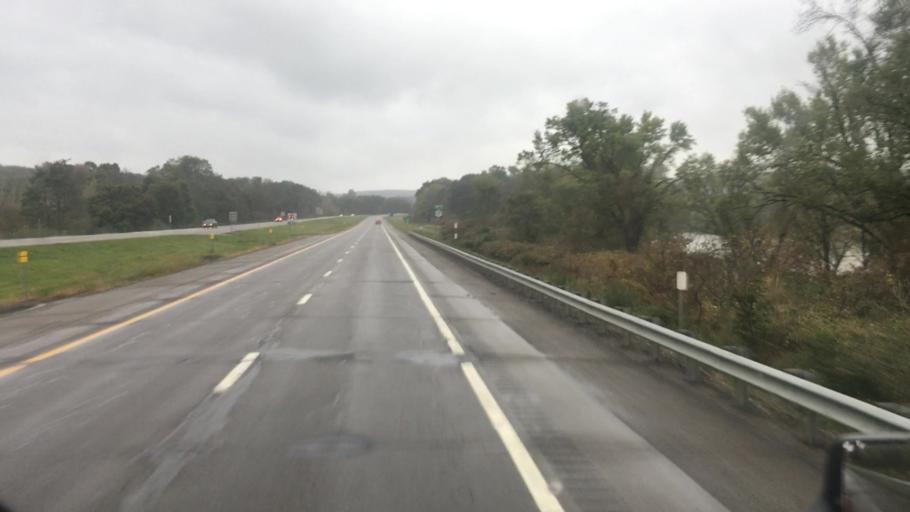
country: US
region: New York
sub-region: Tioga County
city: Apalachin
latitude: 42.0709
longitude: -76.1504
